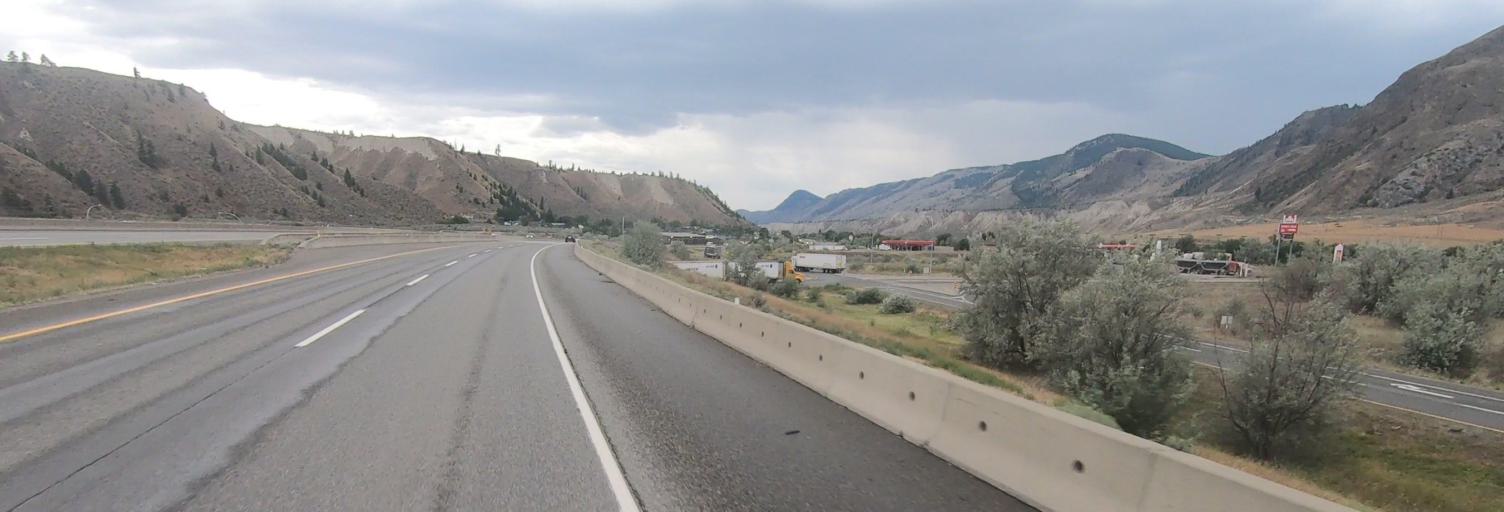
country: CA
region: British Columbia
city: Kamloops
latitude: 50.6597
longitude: -120.1161
